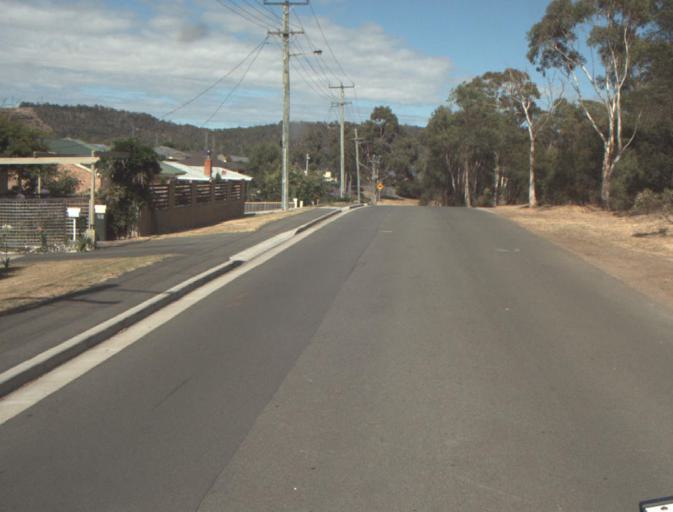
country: AU
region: Tasmania
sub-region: Launceston
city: Summerhill
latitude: -41.4720
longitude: 147.1179
